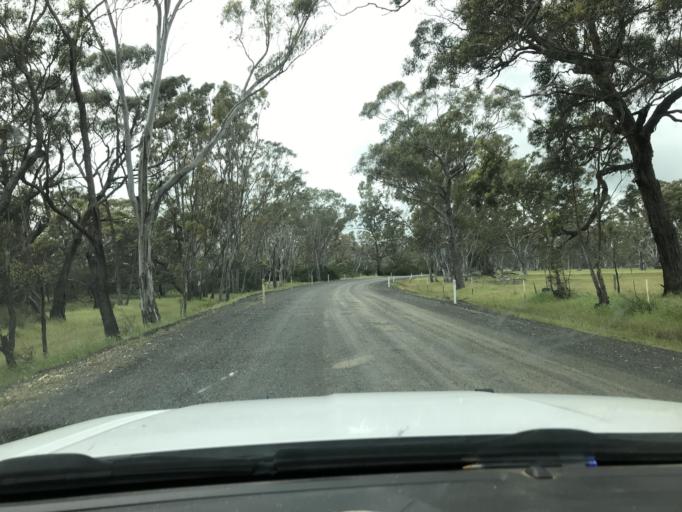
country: AU
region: South Australia
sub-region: Wattle Range
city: Penola
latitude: -37.1768
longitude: 141.4384
